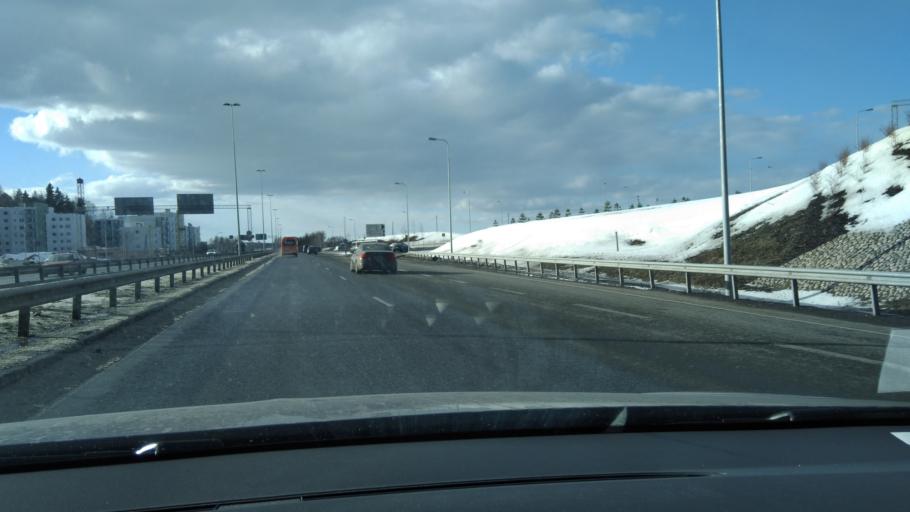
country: FI
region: Pirkanmaa
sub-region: Tampere
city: Tampere
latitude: 61.5032
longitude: 23.7250
